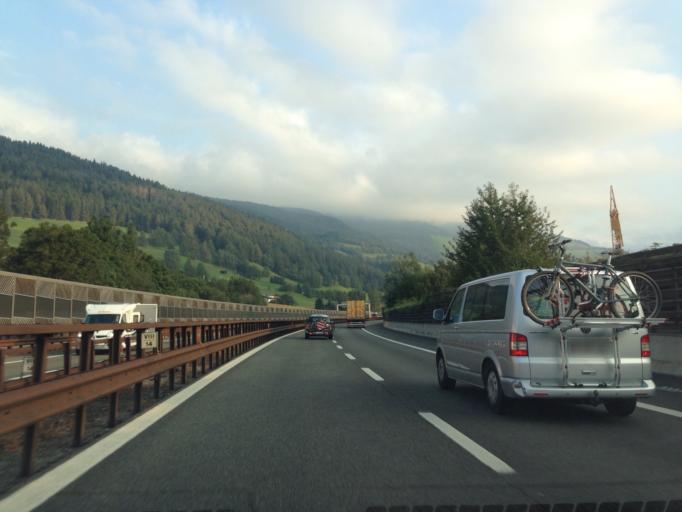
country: IT
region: Trentino-Alto Adige
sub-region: Bolzano
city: Vipiteno
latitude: 46.8907
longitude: 11.4246
